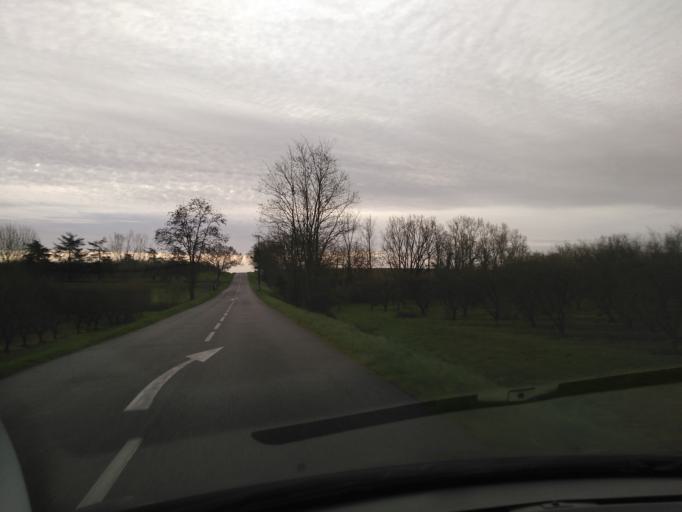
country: FR
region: Midi-Pyrenees
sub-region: Departement du Tarn-et-Garonne
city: Verdun-sur-Garonne
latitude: 43.8190
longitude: 1.1864
